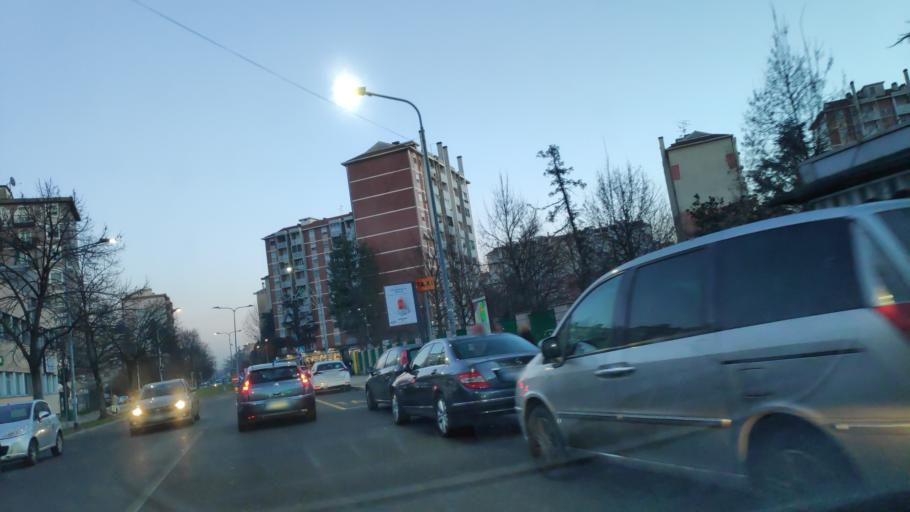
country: IT
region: Lombardy
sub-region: Citta metropolitana di Milano
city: Rozzano
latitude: 45.3835
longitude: 9.1563
